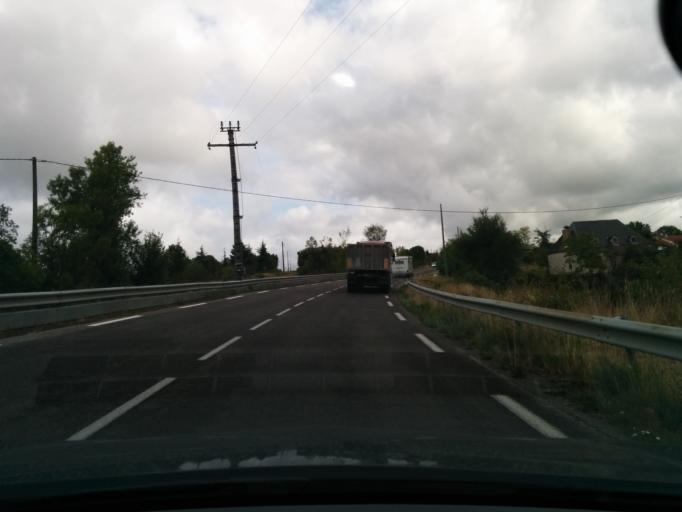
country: FR
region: Midi-Pyrenees
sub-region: Departement du Lot
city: Souillac
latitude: 44.9158
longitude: 1.4838
